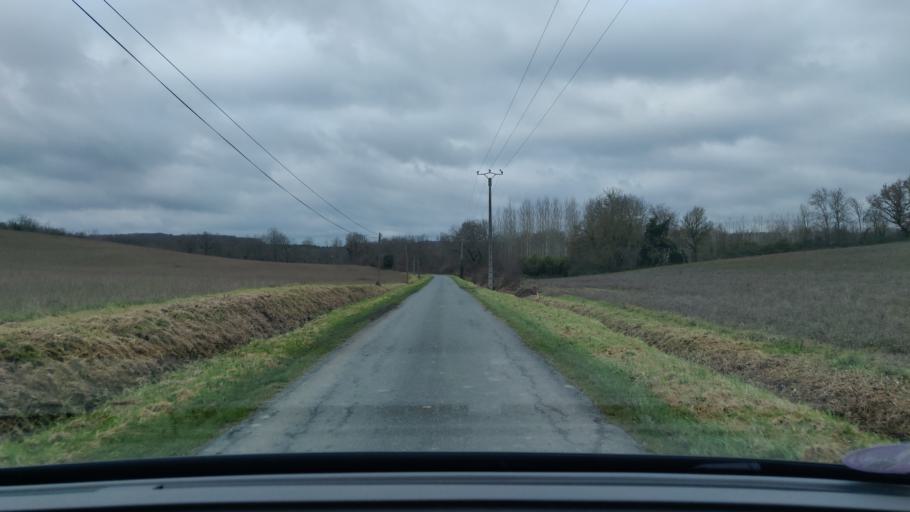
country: FR
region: Aquitaine
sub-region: Departement du Lot-et-Garonne
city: Saint-Hilaire
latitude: 44.5781
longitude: 0.7128
